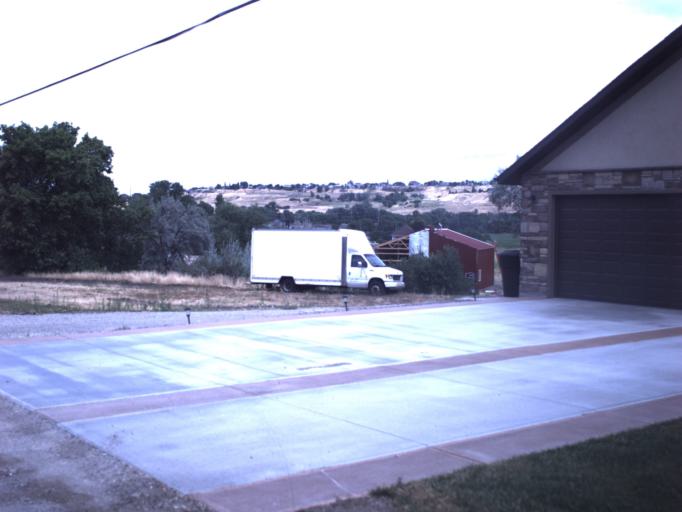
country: US
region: Utah
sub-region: Weber County
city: Washington Terrace
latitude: 41.1436
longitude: -111.9755
